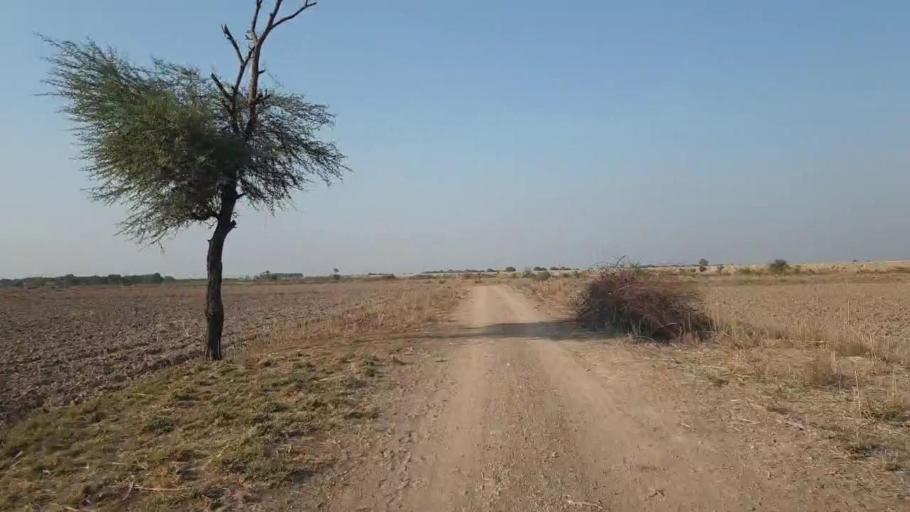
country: PK
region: Sindh
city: Mirpur Khas
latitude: 25.4543
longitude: 68.9332
